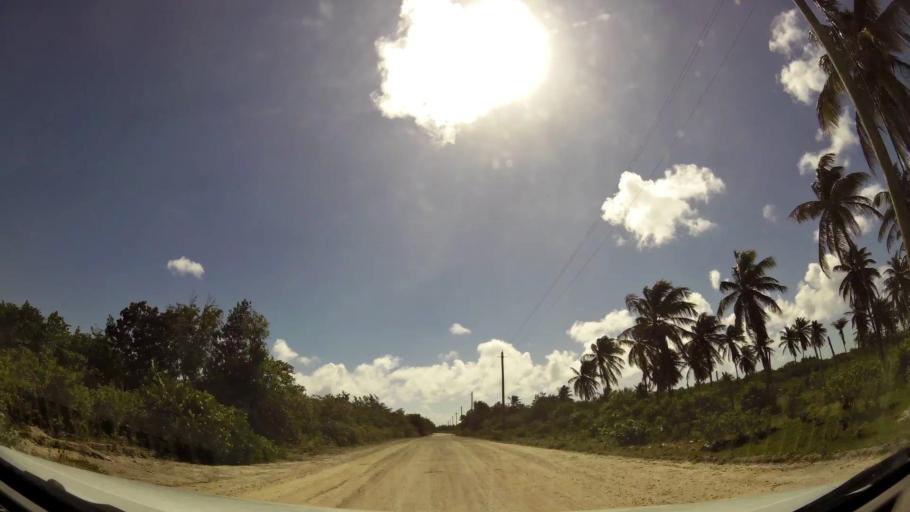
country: AG
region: Barbuda
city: Codrington
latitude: 17.5999
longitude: -61.8291
